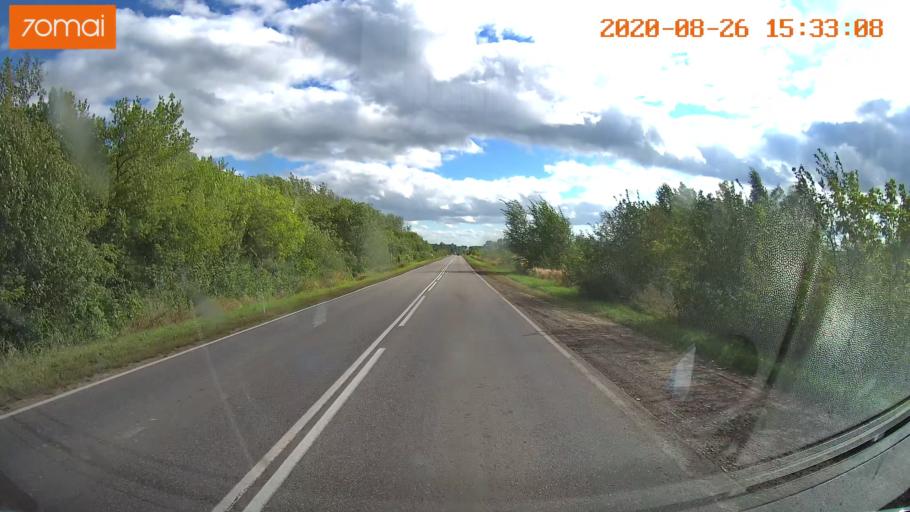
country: RU
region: Tula
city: Severo-Zadonsk
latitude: 54.0710
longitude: 38.3527
